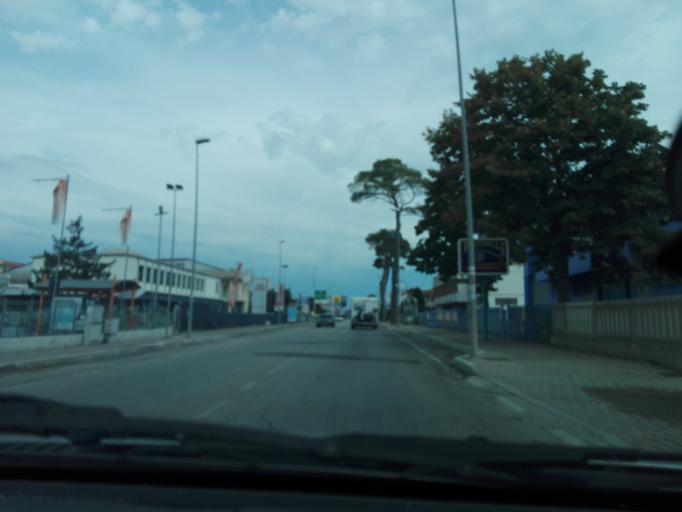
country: IT
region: Abruzzo
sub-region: Provincia di Teramo
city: Silvi
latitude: 42.5371
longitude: 14.1274
